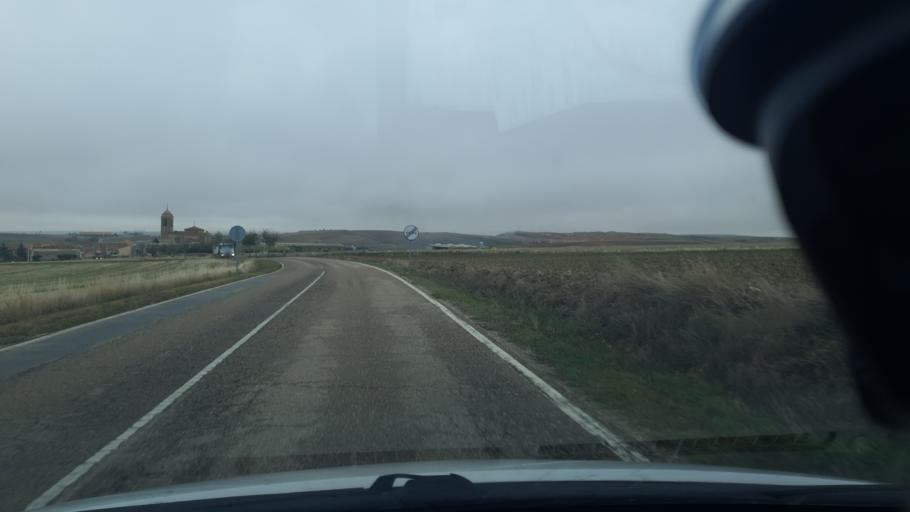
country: ES
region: Castille and Leon
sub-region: Provincia de Segovia
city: Valseca
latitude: 40.9969
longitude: -4.1803
